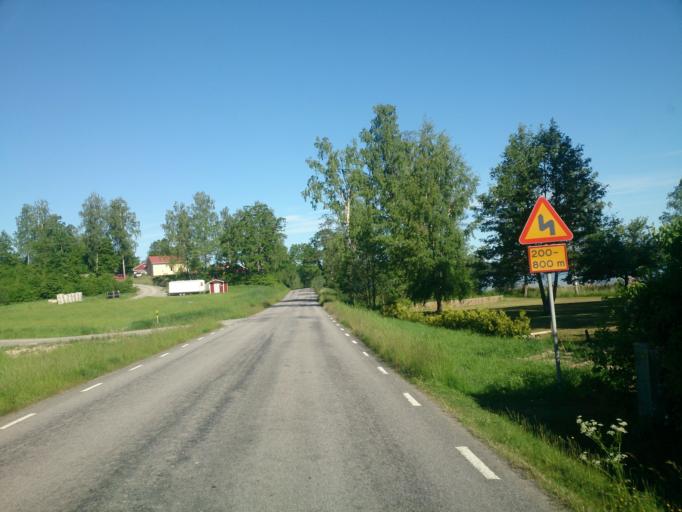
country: SE
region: OEstergoetland
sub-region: Atvidabergs Kommun
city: Atvidaberg
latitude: 58.1815
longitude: 16.0558
